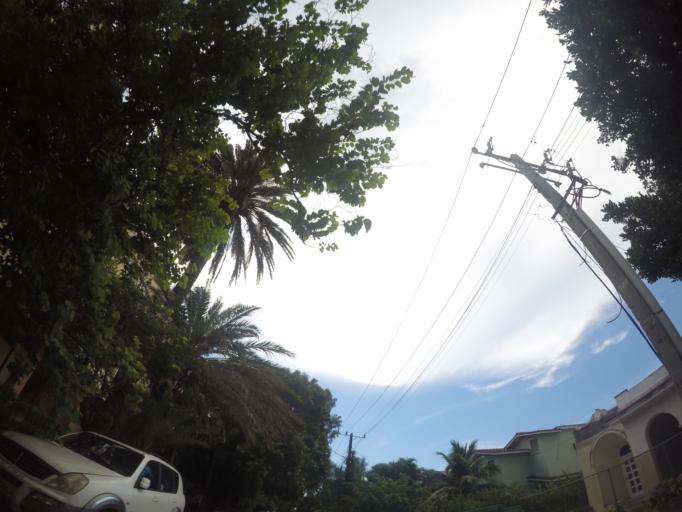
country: CU
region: La Habana
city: Havana
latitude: 23.1211
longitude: -82.4248
